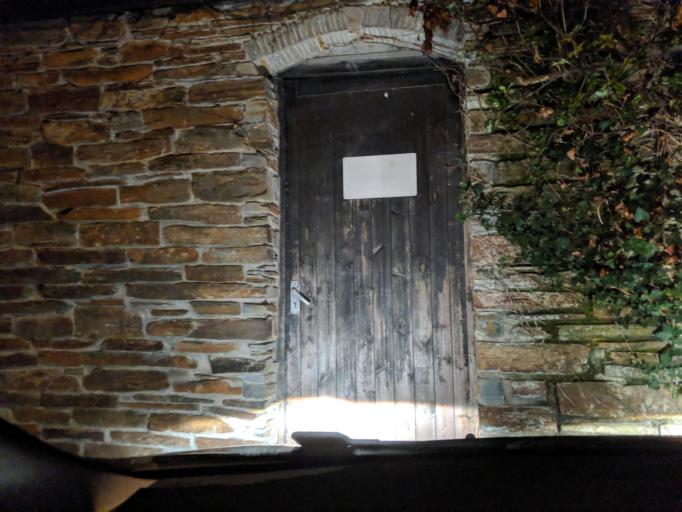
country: GB
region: England
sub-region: Cornwall
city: Mevagissey
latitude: 50.2708
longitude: -4.7878
